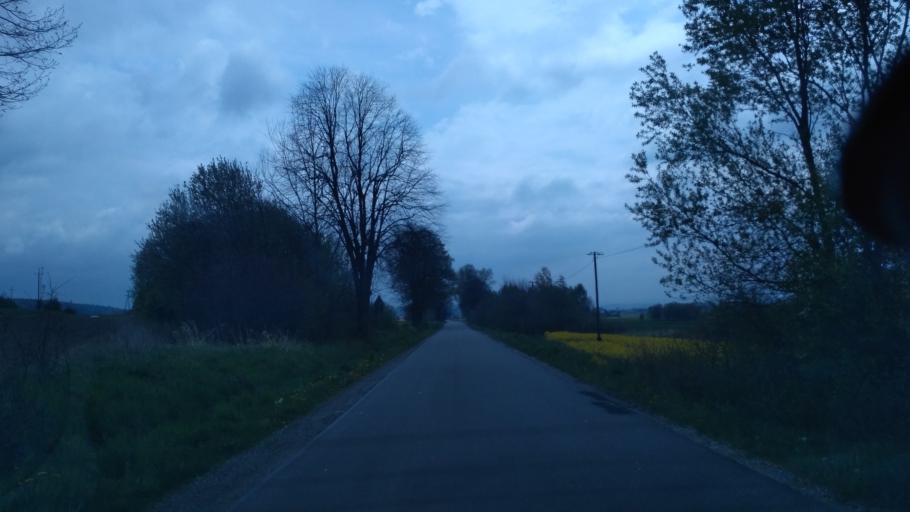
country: PL
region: Subcarpathian Voivodeship
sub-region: Powiat brzozowski
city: Jablonica Polska
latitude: 49.6885
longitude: 21.8924
